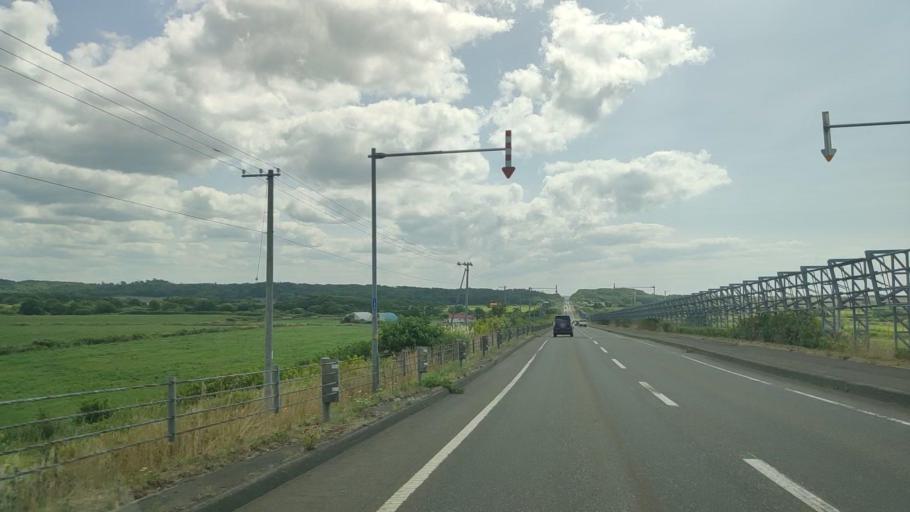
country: JP
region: Hokkaido
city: Makubetsu
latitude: 44.7781
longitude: 141.7914
